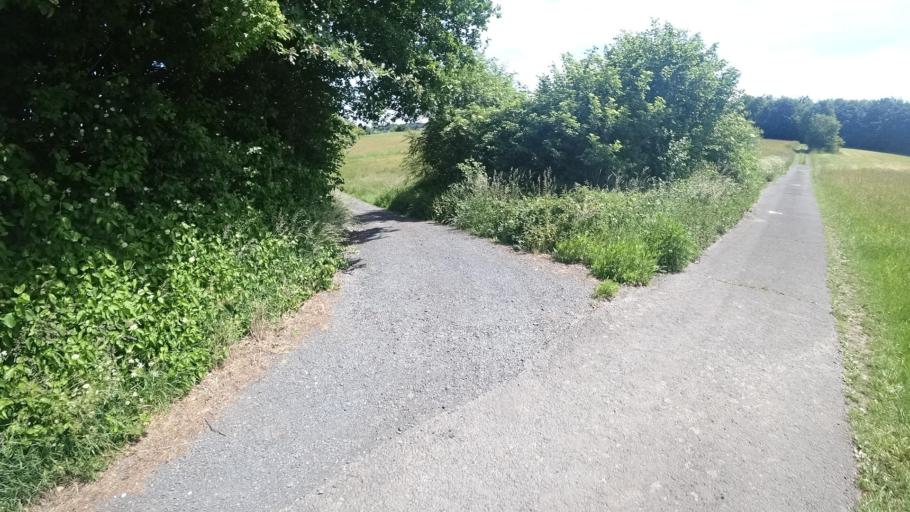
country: DE
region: Rheinland-Pfalz
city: Sorth
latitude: 50.6967
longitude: 7.6789
